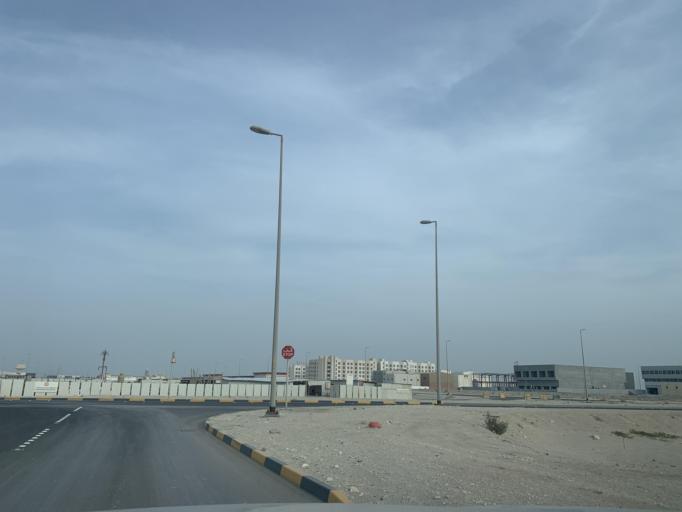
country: BH
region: Muharraq
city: Al Muharraq
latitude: 26.3121
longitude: 50.6193
